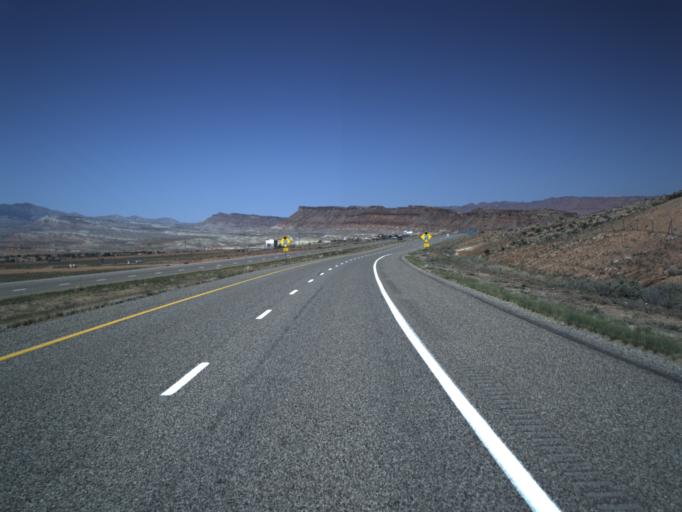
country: US
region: Utah
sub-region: Washington County
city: Saint George
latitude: 37.0190
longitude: -113.5975
